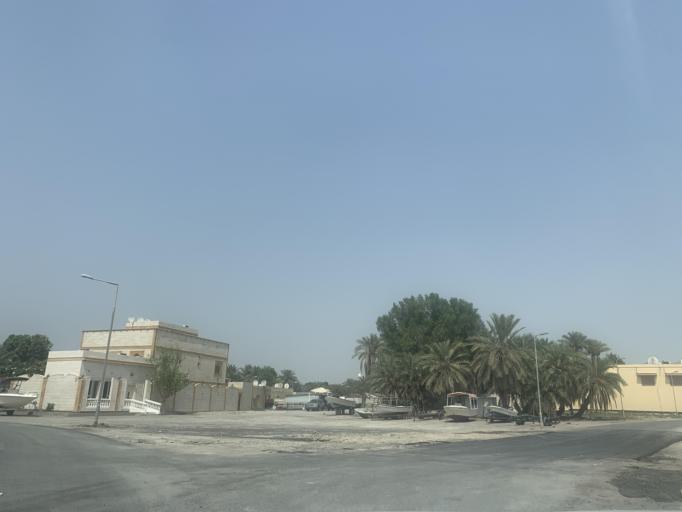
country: BH
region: Central Governorate
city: Madinat Hamad
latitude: 26.1640
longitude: 50.4485
